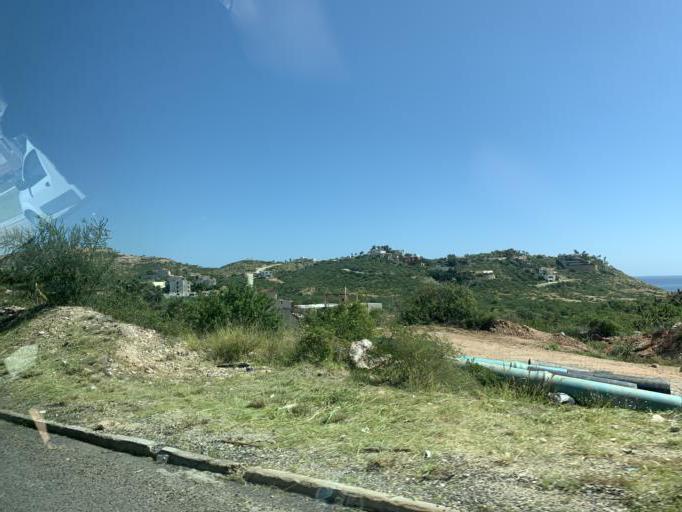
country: MX
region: Baja California Sur
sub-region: Los Cabos
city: San Jose del Cabo
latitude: 22.9979
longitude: -109.7364
